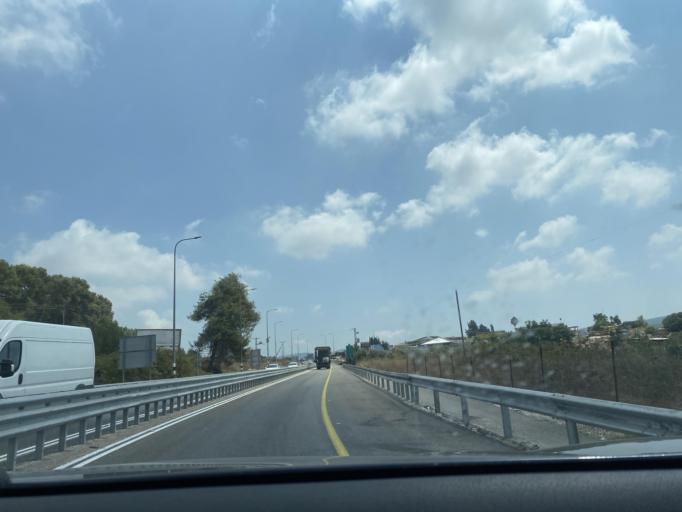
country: IL
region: Northern District
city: Kefar Weradim
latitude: 33.0042
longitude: 35.2965
